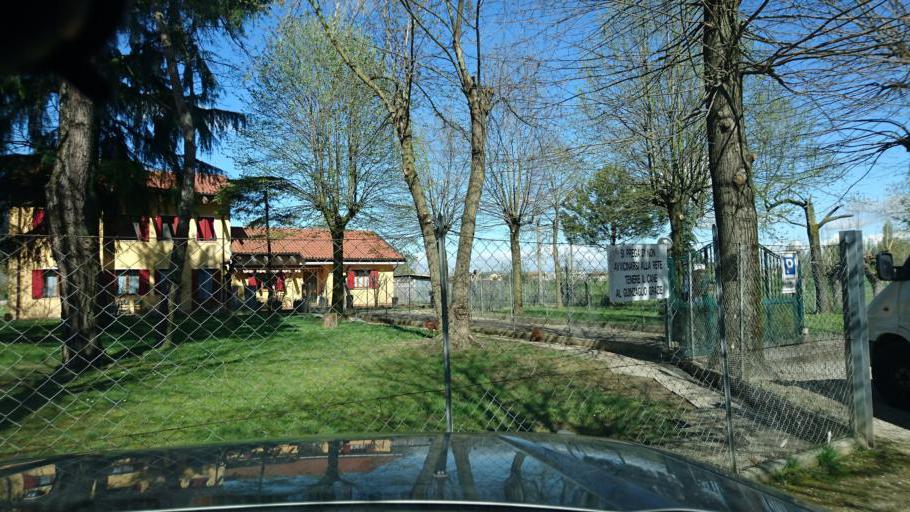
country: IT
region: Veneto
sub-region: Provincia di Padova
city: Mejaniga
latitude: 45.4623
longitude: 11.9070
